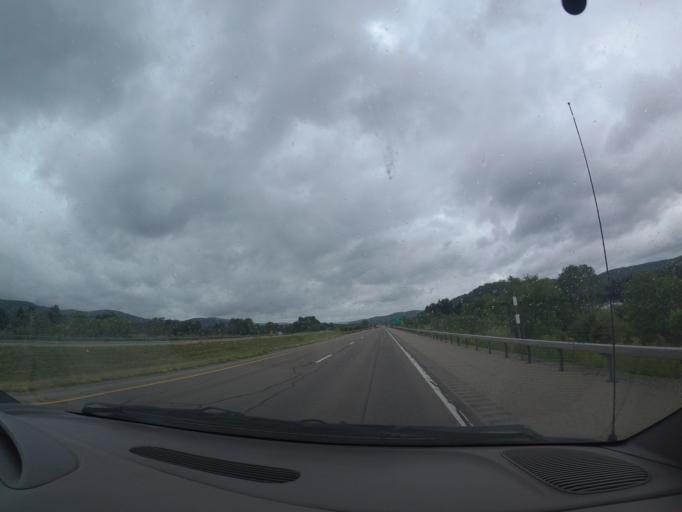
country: US
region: New York
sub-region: Cattaraugus County
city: Allegany
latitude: 42.1029
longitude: -78.4971
